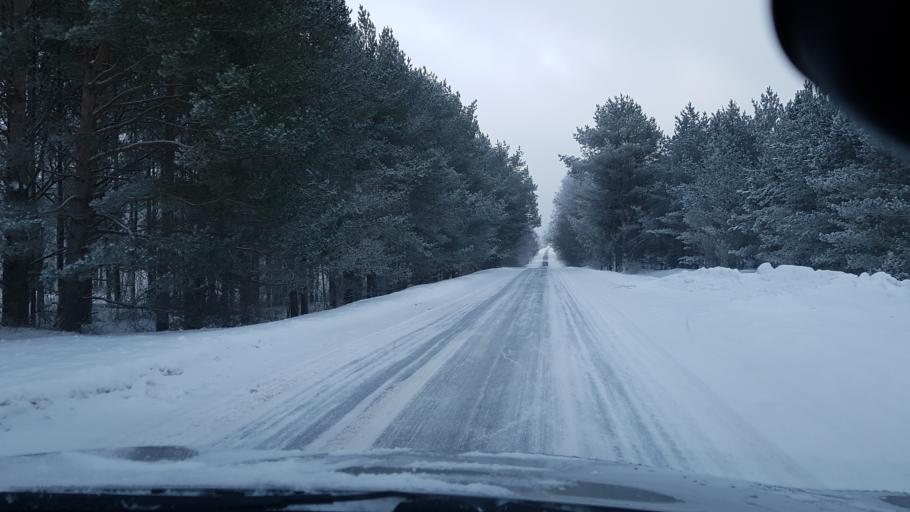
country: EE
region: Harju
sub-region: Keila linn
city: Keila
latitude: 59.3331
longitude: 24.3993
